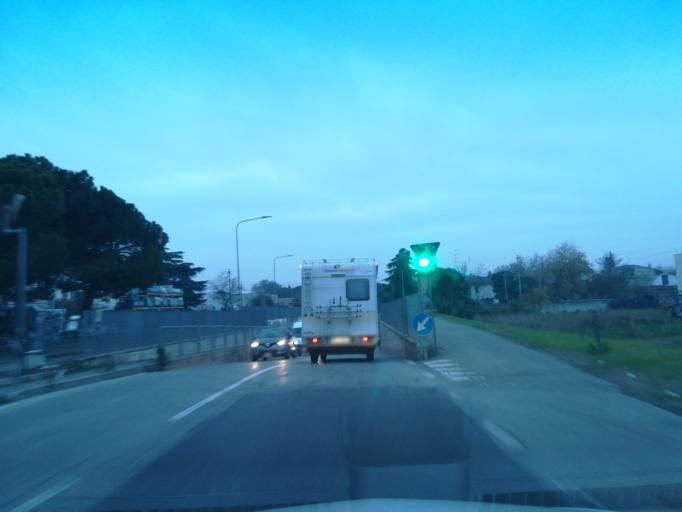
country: IT
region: Emilia-Romagna
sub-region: Provincia di Ravenna
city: Faenza
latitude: 44.3005
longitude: 11.8690
